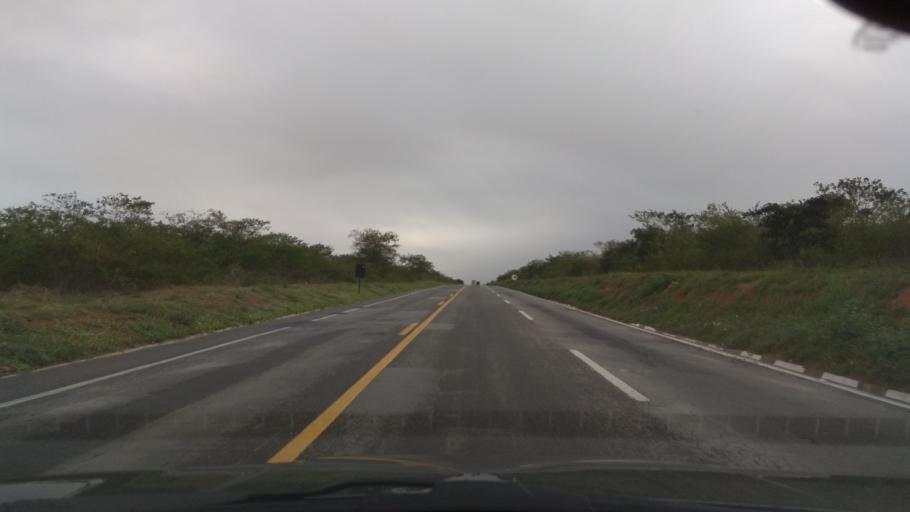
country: BR
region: Bahia
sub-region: Santa Ines
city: Santa Ines
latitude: -13.0308
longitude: -39.9632
